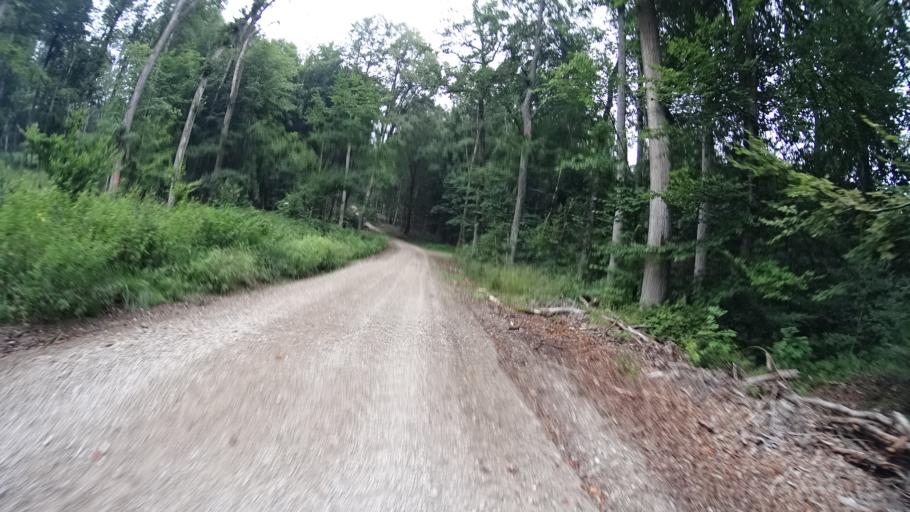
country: DE
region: Bavaria
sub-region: Upper Bavaria
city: Stammham
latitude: 48.8400
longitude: 11.4859
